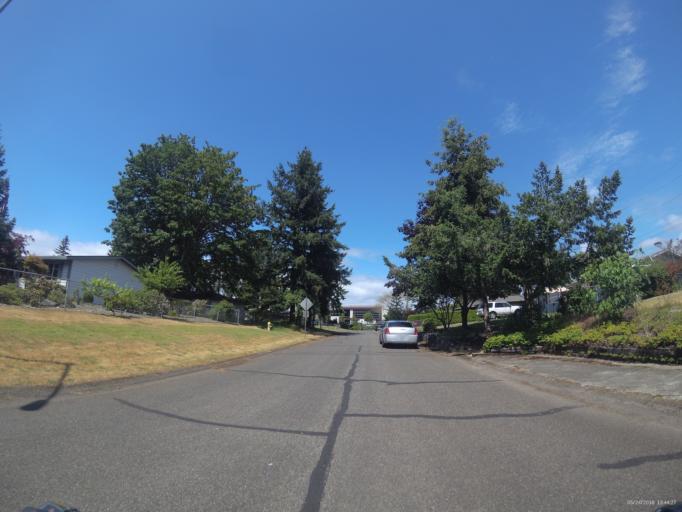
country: US
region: Washington
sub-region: Pierce County
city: Steilacoom
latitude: 47.1779
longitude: -122.5751
